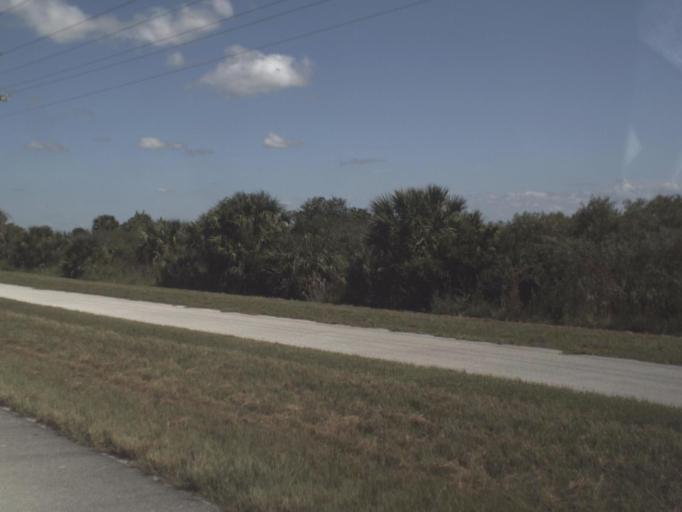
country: US
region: Florida
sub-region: Glades County
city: Moore Haven
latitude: 26.9613
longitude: -81.1214
